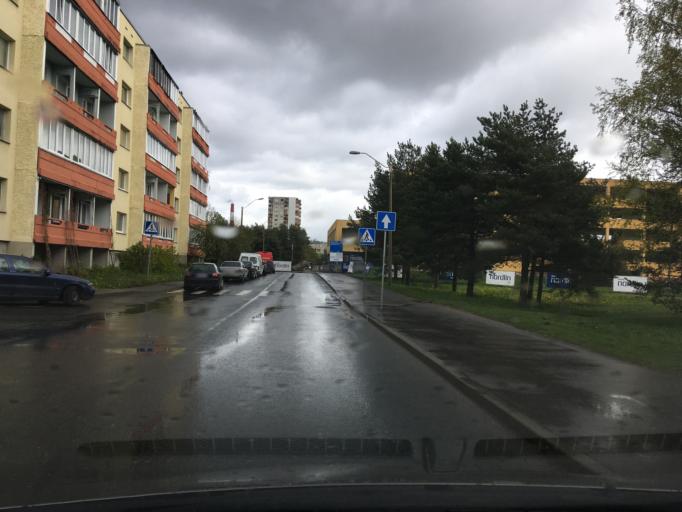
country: EE
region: Harju
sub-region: Tallinna linn
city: Kose
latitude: 59.4432
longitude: 24.8950
